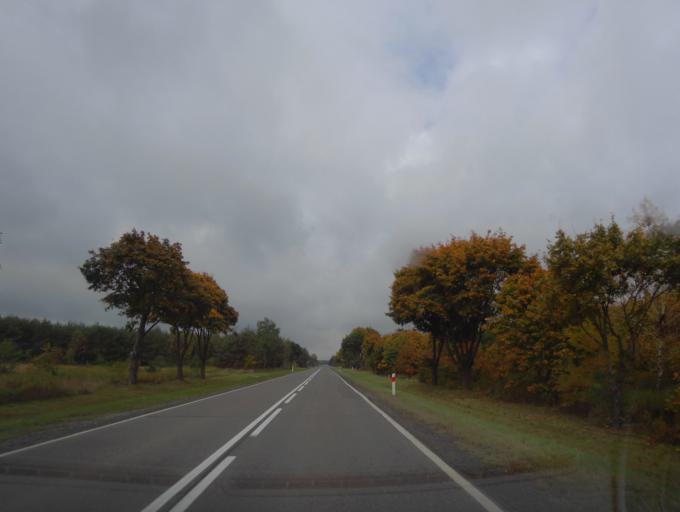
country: PL
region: Subcarpathian Voivodeship
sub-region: Powiat nizanski
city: Przedzel
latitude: 50.4891
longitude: 22.2172
